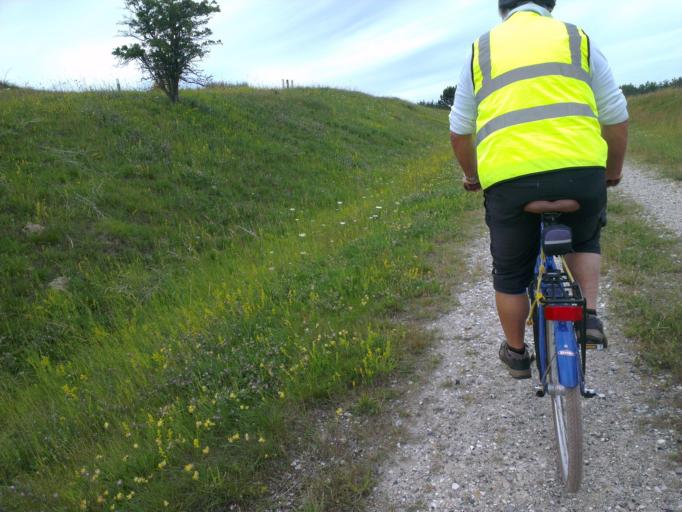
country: DK
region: Capital Region
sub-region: Frederikssund Kommune
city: Jaegerspris
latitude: 55.8965
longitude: 11.9315
